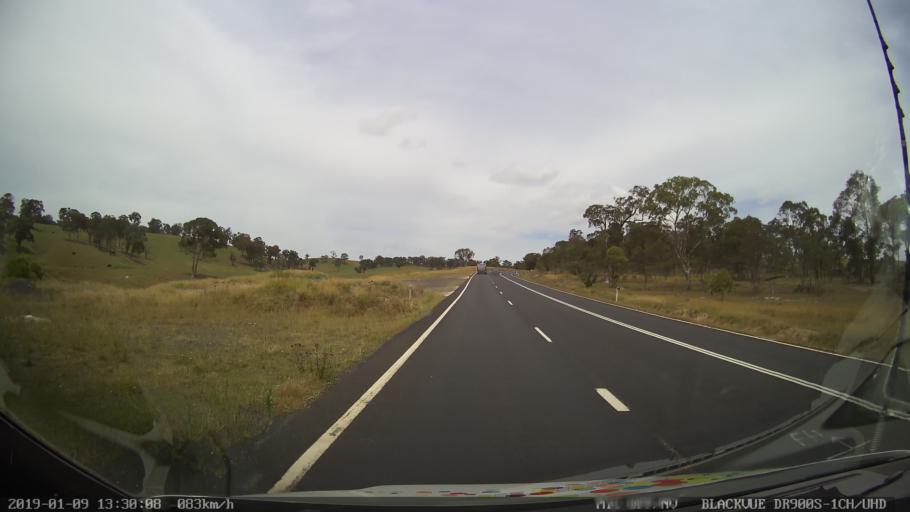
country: AU
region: New South Wales
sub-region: Armidale Dumaresq
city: Enmore
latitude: -30.5146
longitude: 151.9922
